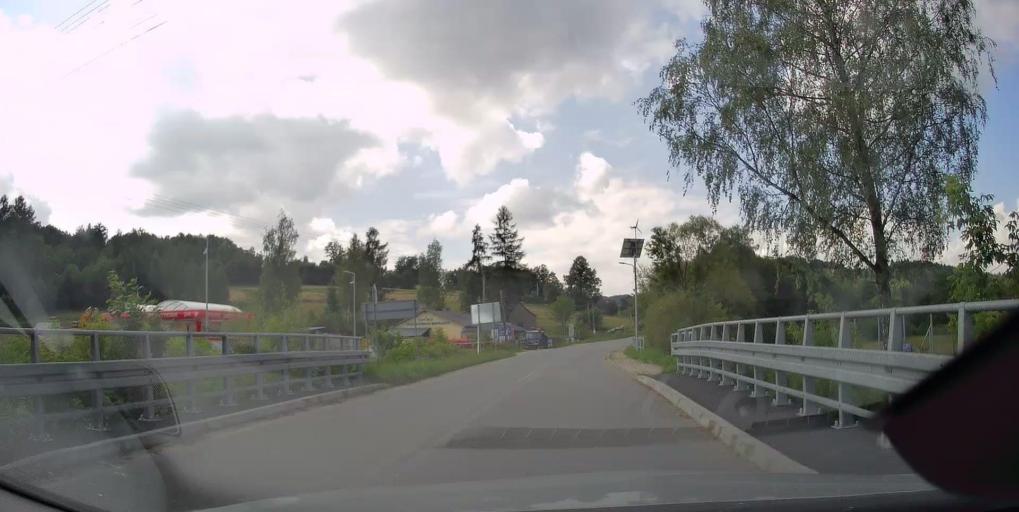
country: PL
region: Lesser Poland Voivodeship
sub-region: Powiat nowosadecki
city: Korzenna
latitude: 49.7546
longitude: 20.7768
